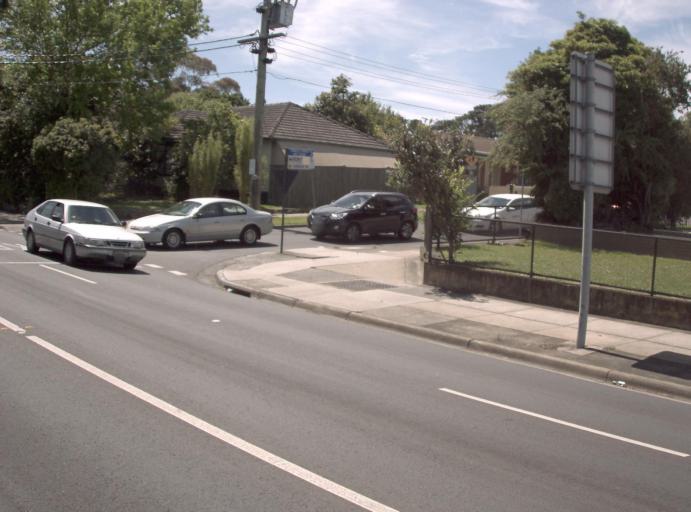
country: AU
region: Victoria
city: Burwood East
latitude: -37.8714
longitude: 145.1485
